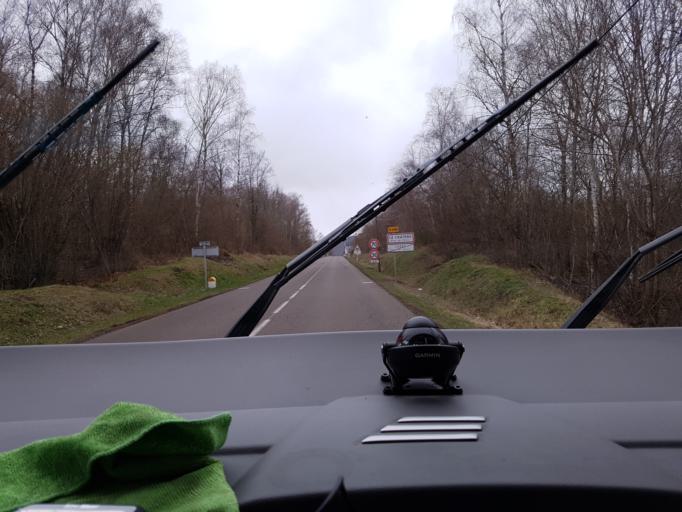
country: FR
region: Auvergne
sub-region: Departement du Puy-de-Dome
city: Volvic
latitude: 45.8603
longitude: 3.0098
